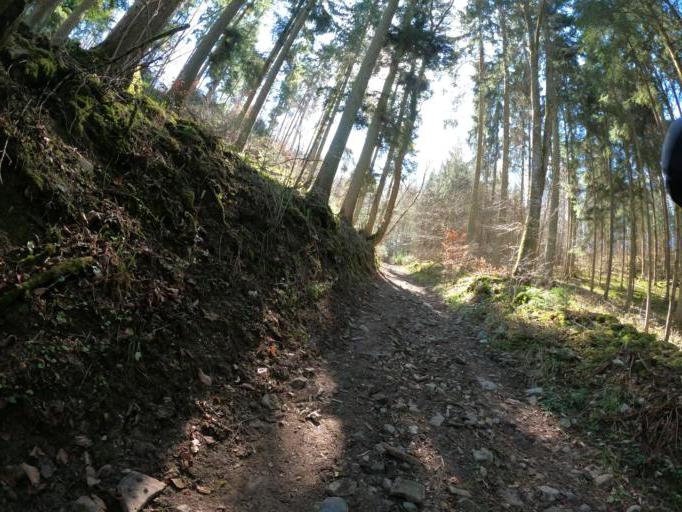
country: DE
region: Baden-Wuerttemberg
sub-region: Regierungsbezirk Stuttgart
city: Bondorf
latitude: 48.4674
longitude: 8.8458
